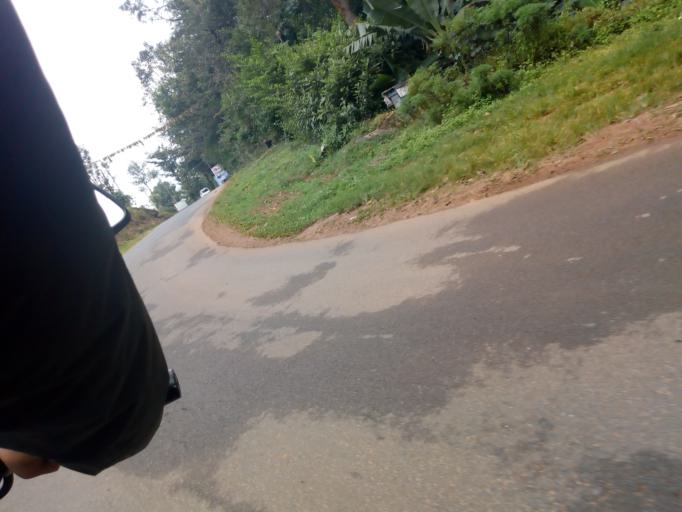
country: IN
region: Karnataka
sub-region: Dakshina Kannada
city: Sulya
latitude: 12.3844
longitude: 75.5142
